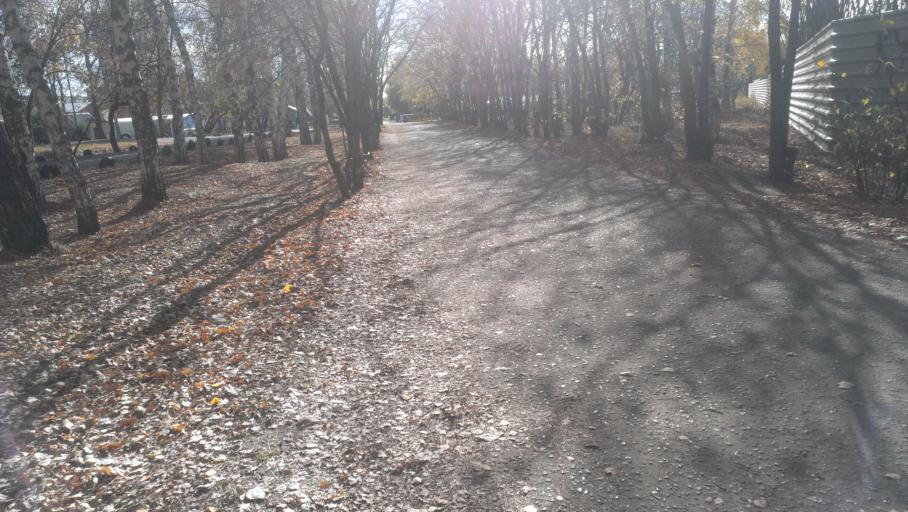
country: RU
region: Altai Krai
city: Novosilikatnyy
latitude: 53.3591
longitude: 83.6850
